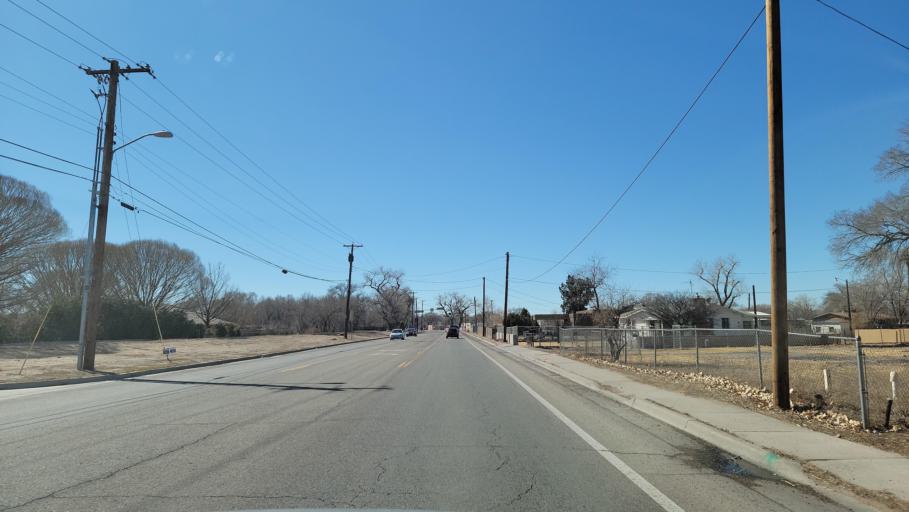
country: US
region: New Mexico
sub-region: Bernalillo County
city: South Valley
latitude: 35.0135
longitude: -106.6863
